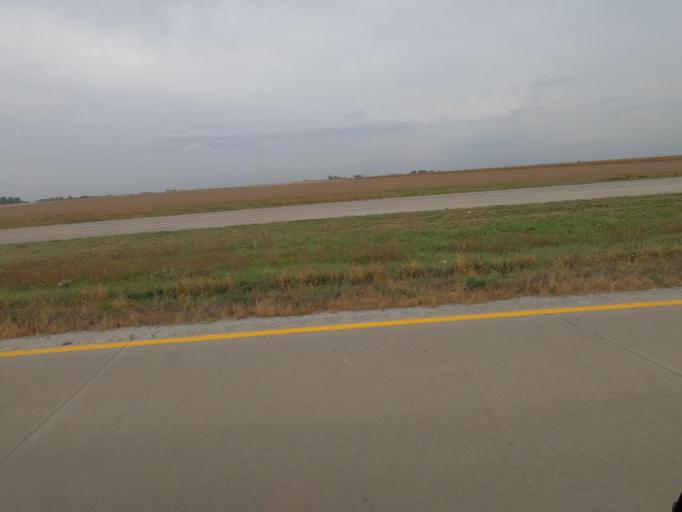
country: US
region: Iowa
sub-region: Marion County
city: Pella
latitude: 41.3690
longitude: -92.7968
